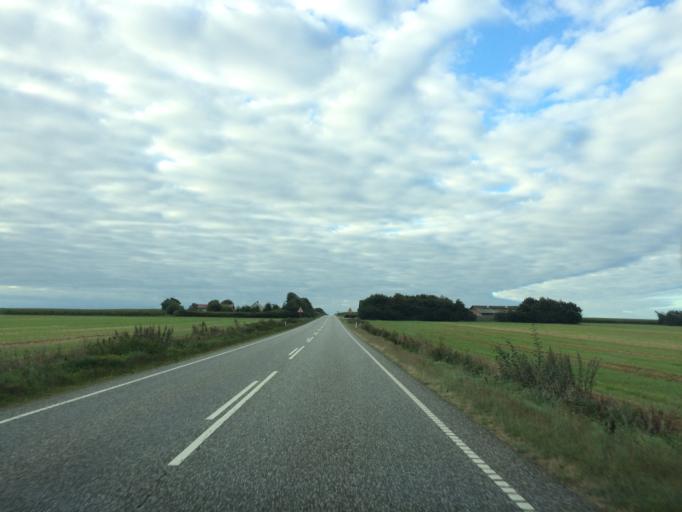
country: DK
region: Central Jutland
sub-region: Ringkobing-Skjern Kommune
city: Skjern
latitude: 56.0286
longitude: 8.5020
